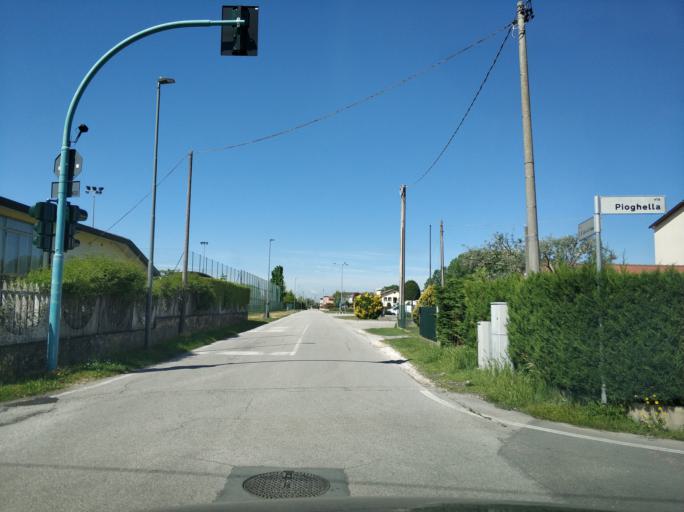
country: IT
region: Veneto
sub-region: Provincia di Venezia
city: Fiesso d'Artico
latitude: 45.4192
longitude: 12.0224
